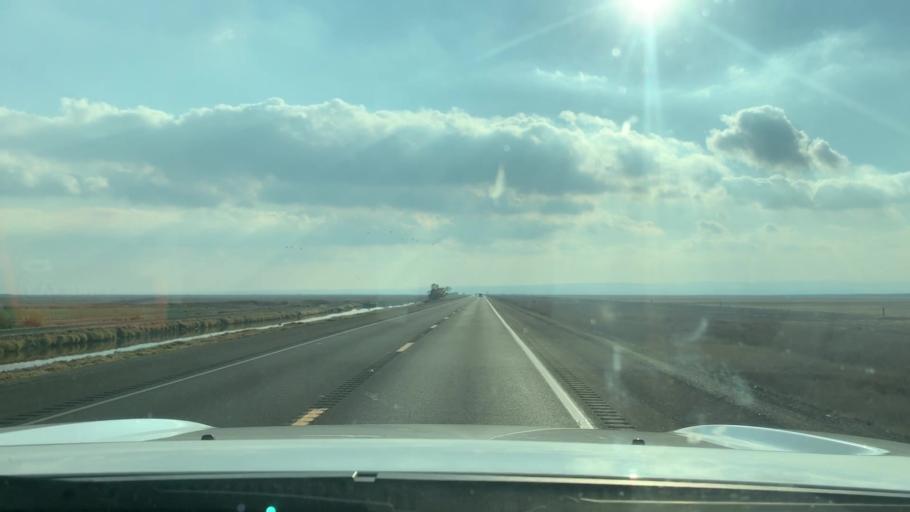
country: US
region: California
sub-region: Kings County
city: Stratford
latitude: 36.1114
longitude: -119.8997
